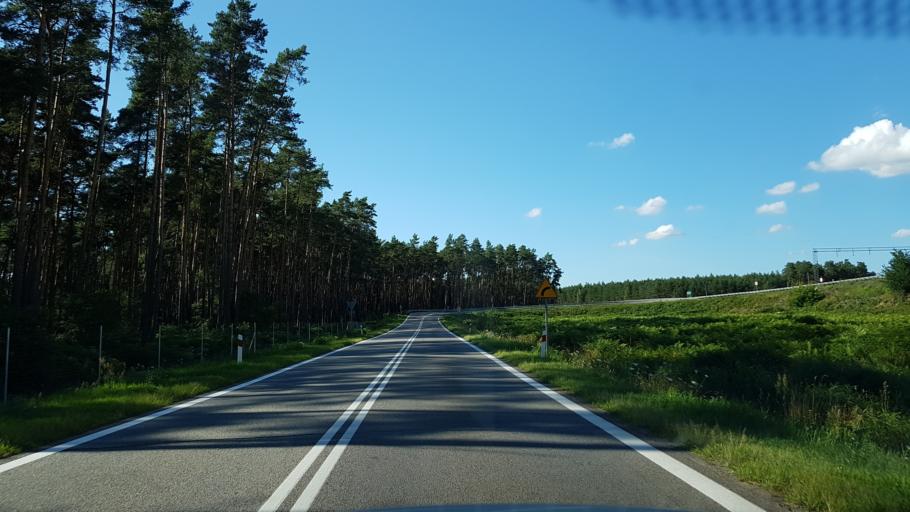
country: PL
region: West Pomeranian Voivodeship
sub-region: Powiat goleniowski
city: Goleniow
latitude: 53.5319
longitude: 14.8100
